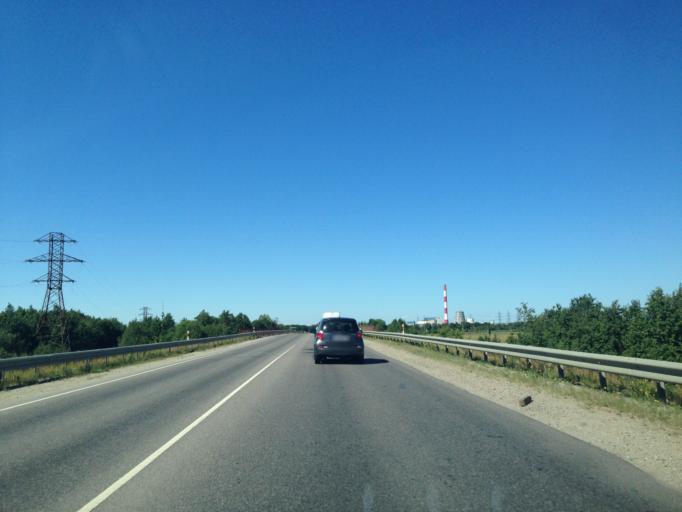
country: EE
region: Harju
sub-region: Joelaehtme vald
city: Loo
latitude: 59.4244
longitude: 24.9211
